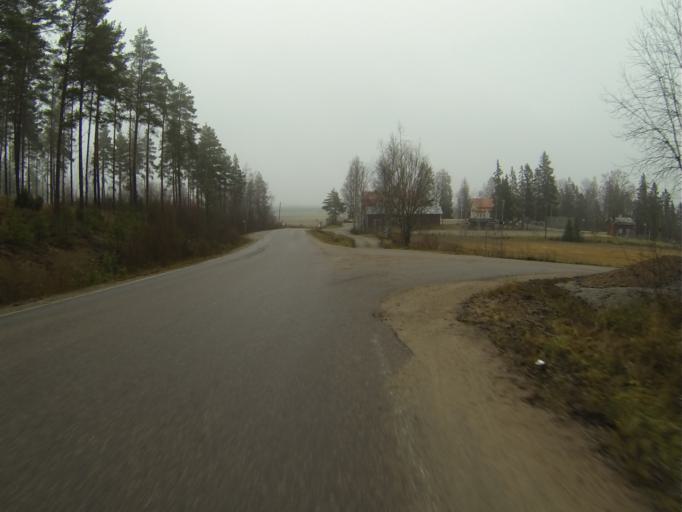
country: FI
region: Varsinais-Suomi
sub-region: Salo
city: Halikko
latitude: 60.4162
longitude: 22.9460
